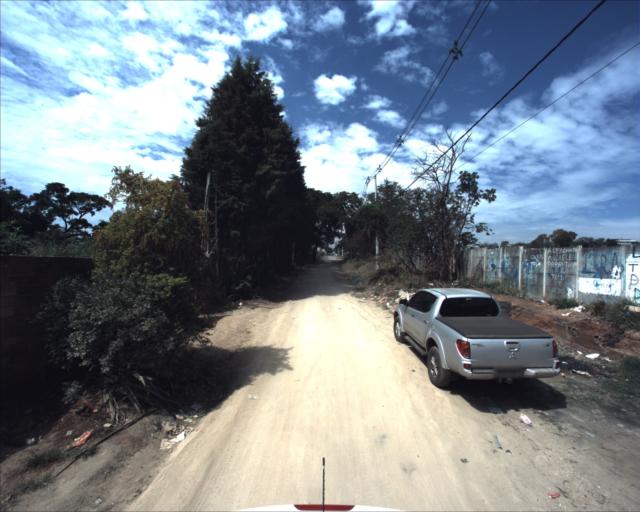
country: BR
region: Sao Paulo
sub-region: Sorocaba
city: Sorocaba
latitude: -23.4843
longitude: -47.5026
